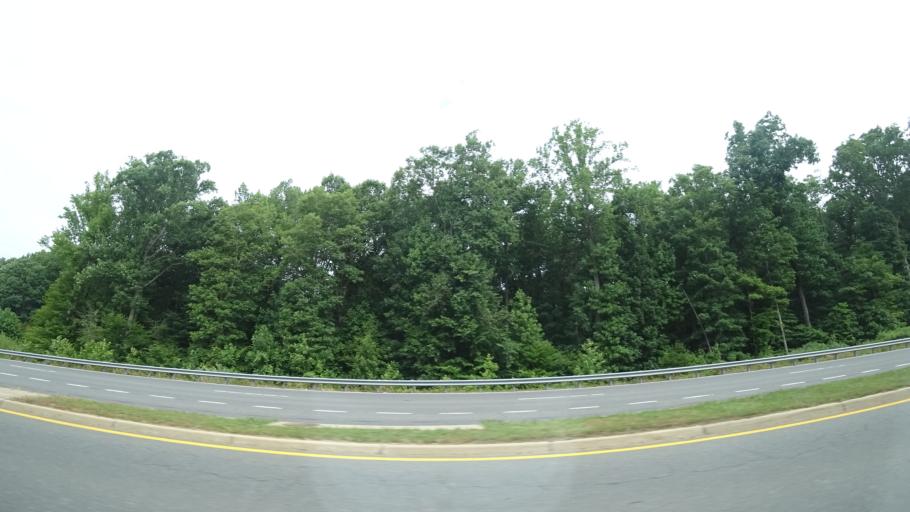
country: US
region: Virginia
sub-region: Spotsylvania County
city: Spotsylvania
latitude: 38.2033
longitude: -77.6042
